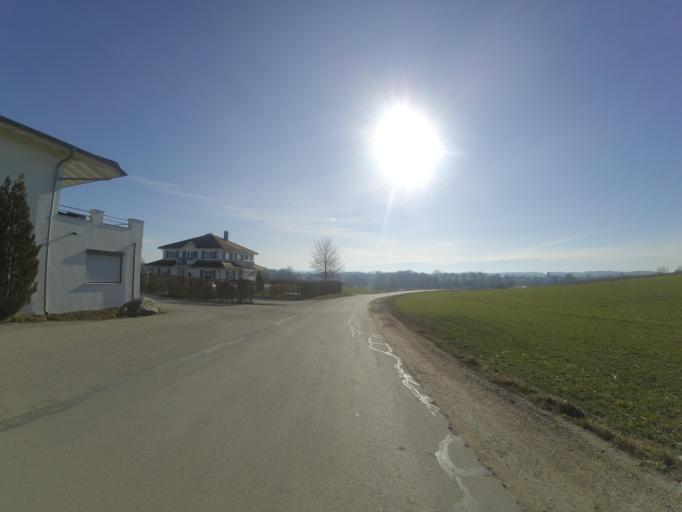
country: DE
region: Baden-Wuerttemberg
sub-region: Tuebingen Region
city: Aulendorf
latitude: 47.9372
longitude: 9.6375
